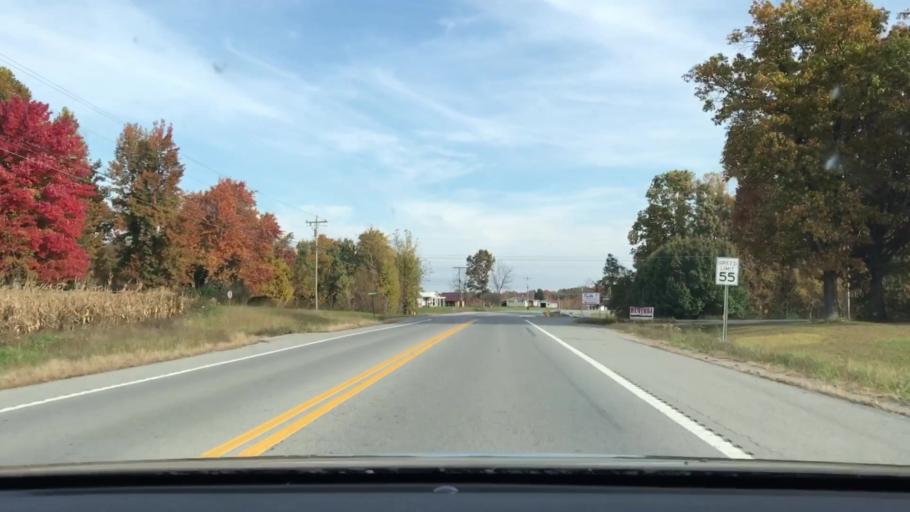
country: US
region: Tennessee
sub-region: Fentress County
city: Grimsley
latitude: 36.2781
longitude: -84.9819
